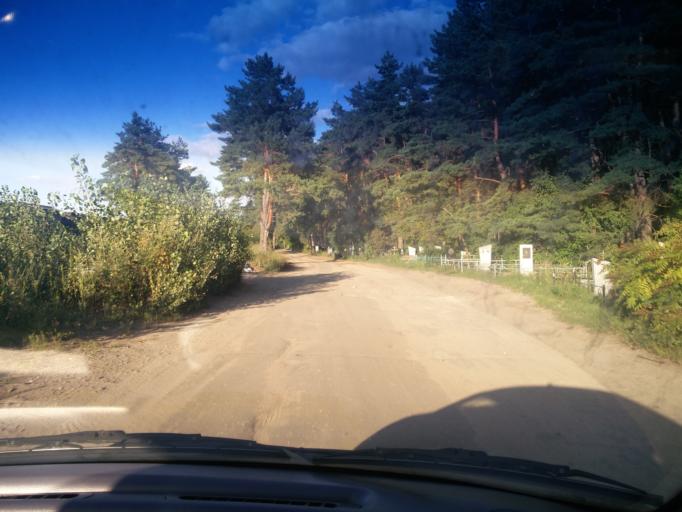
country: RU
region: Voronezj
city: Pridonskoy
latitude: 51.6696
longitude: 39.1016
